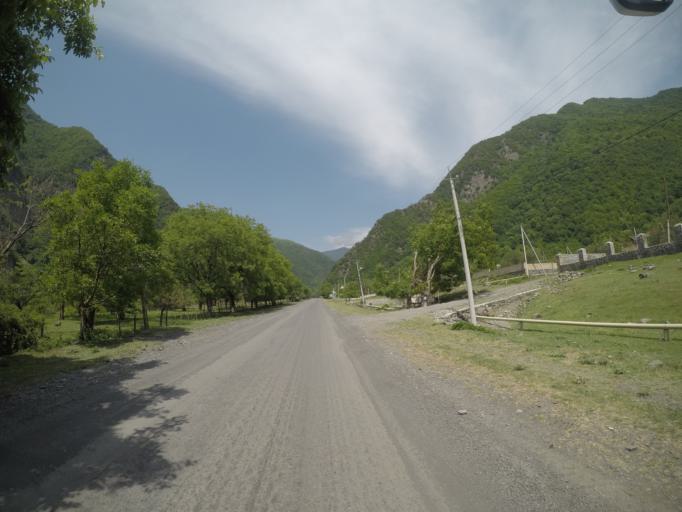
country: AZ
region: Qakh Rayon
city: Qaxbas
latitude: 41.4590
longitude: 47.0265
